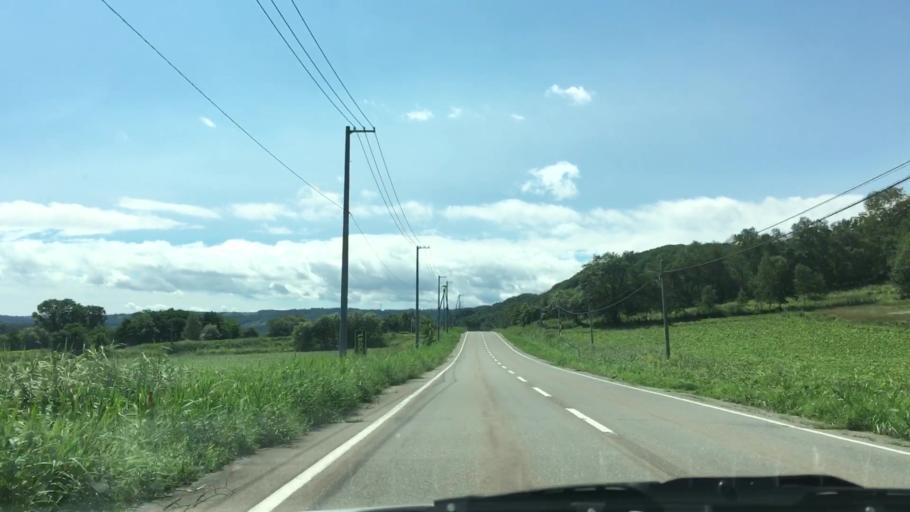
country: JP
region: Hokkaido
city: Otofuke
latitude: 43.2603
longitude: 143.5749
